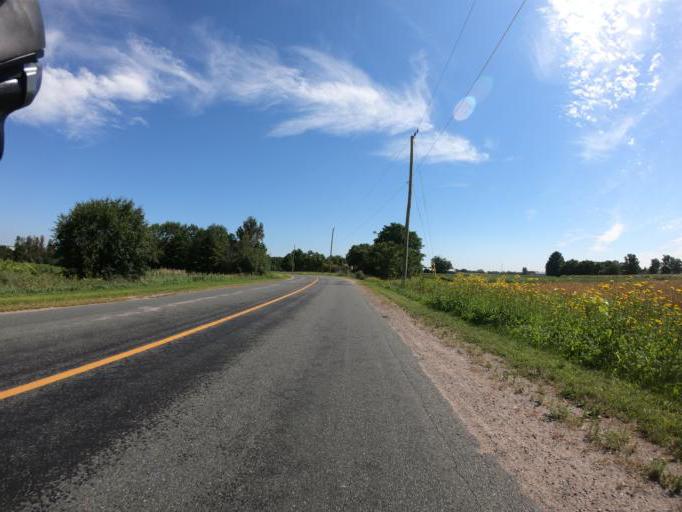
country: CA
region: Ontario
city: Waterloo
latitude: 43.4992
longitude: -80.4219
